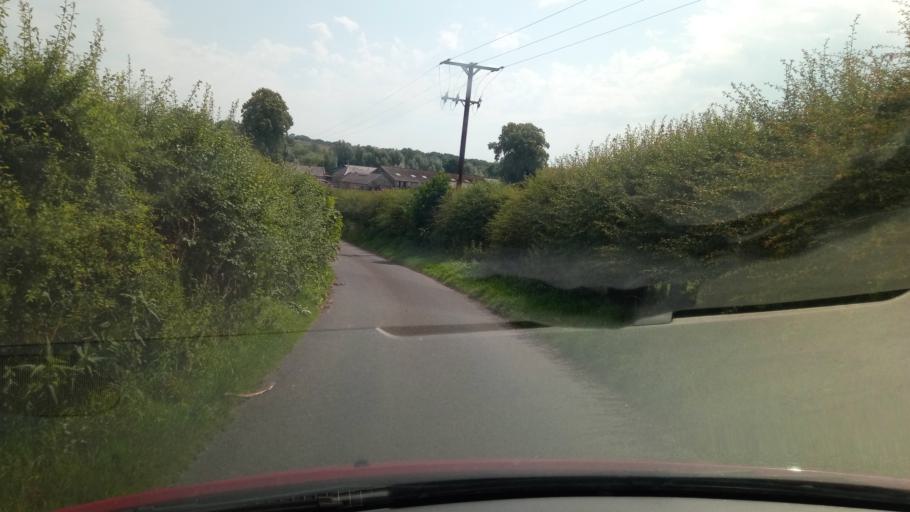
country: GB
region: Scotland
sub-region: The Scottish Borders
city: Kelso
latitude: 55.5743
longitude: -2.4714
